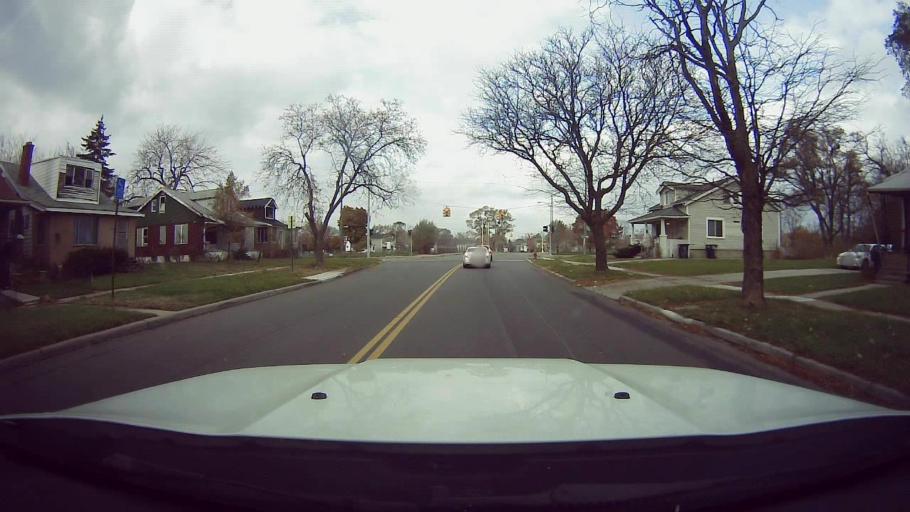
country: US
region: Michigan
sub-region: Wayne County
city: Highland Park
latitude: 42.4038
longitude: -83.1356
